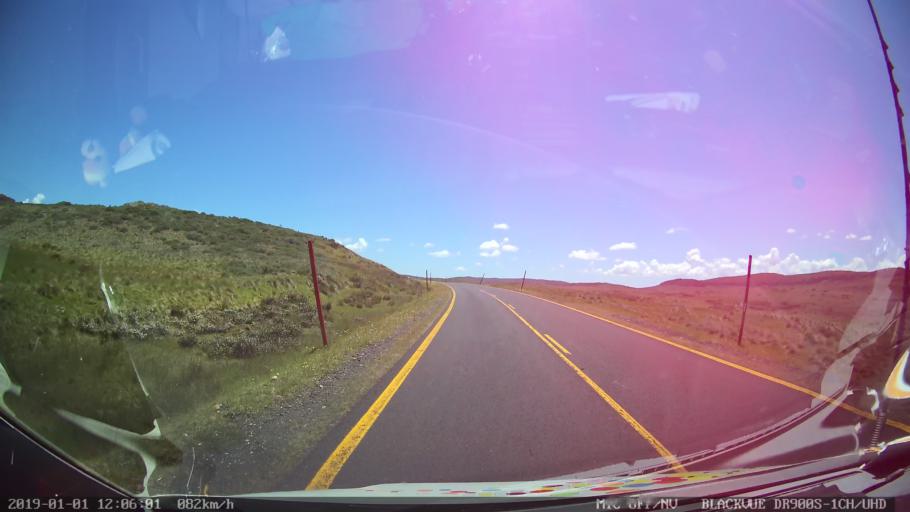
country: AU
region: New South Wales
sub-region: Snowy River
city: Jindabyne
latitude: -35.8502
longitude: 148.4910
